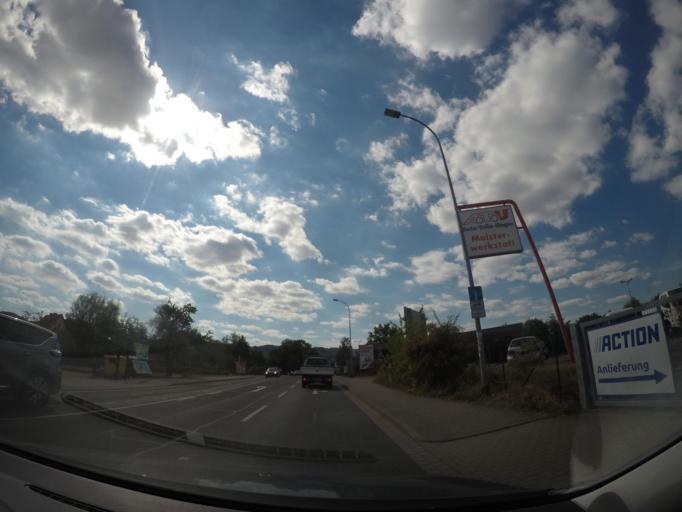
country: DE
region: Saxony-Anhalt
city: Wernigerode
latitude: 51.8436
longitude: 10.7826
